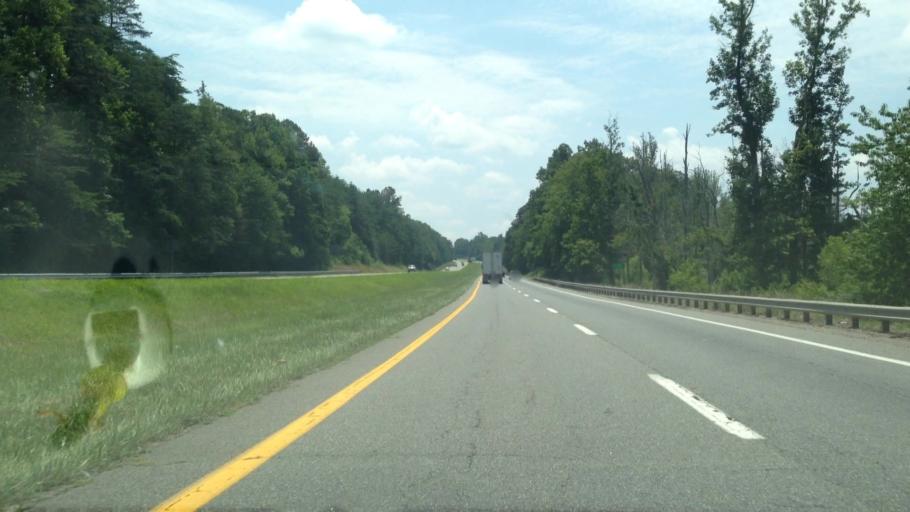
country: US
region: Virginia
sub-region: Henry County
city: Horse Pasture
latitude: 36.6589
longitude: -79.9256
